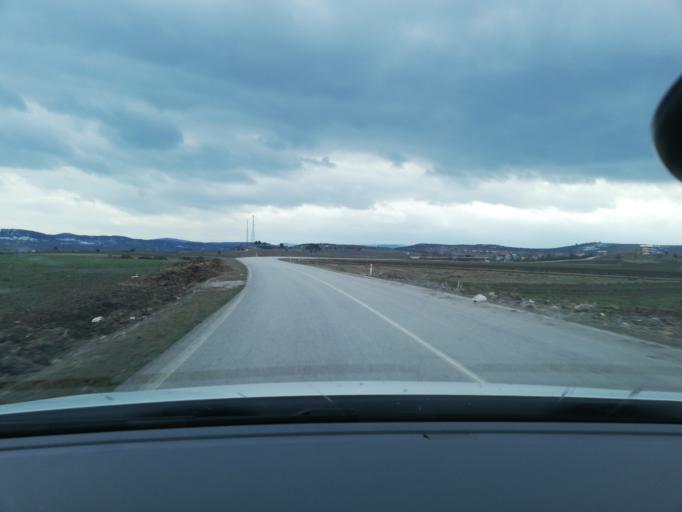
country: TR
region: Bolu
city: Gerede
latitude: 40.6970
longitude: 32.2203
